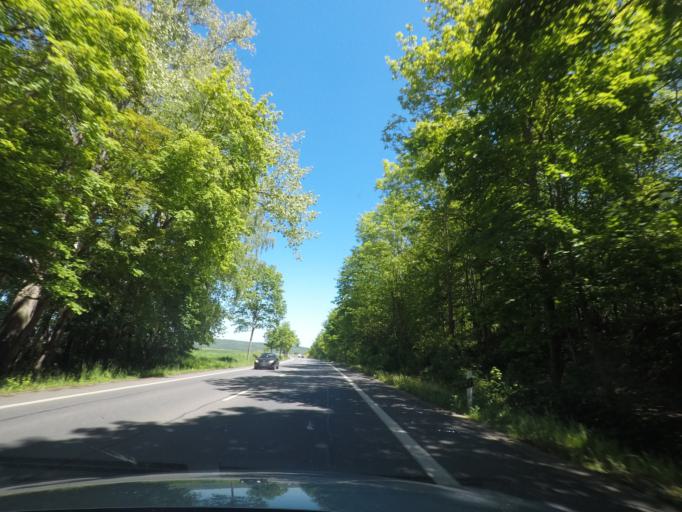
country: DE
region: Lower Saxony
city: Goslar
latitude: 51.9289
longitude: 10.4555
